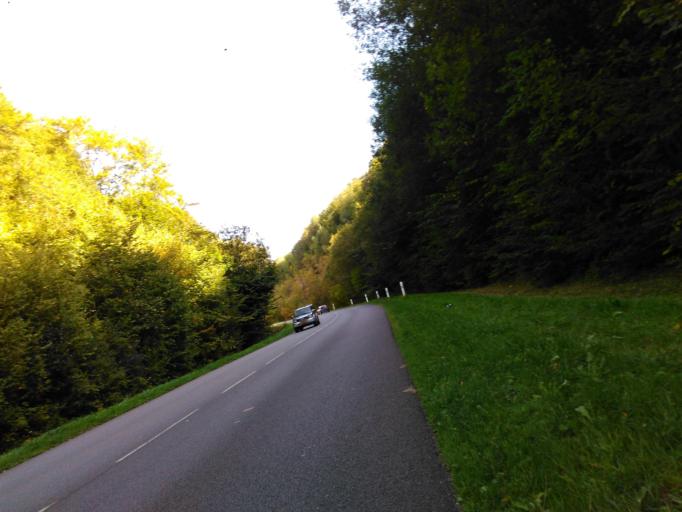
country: FR
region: Lorraine
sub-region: Departement de la Moselle
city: Ottange
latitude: 49.4402
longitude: 6.0279
